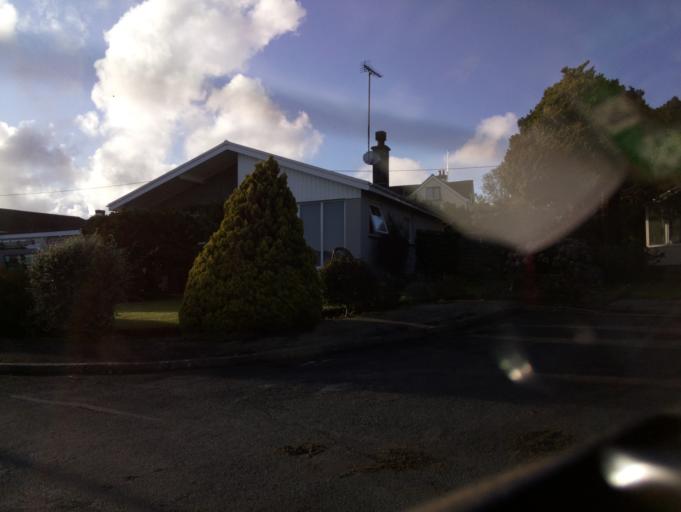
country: GB
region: England
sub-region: Devon
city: Dartmouth
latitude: 50.3279
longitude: -3.5991
